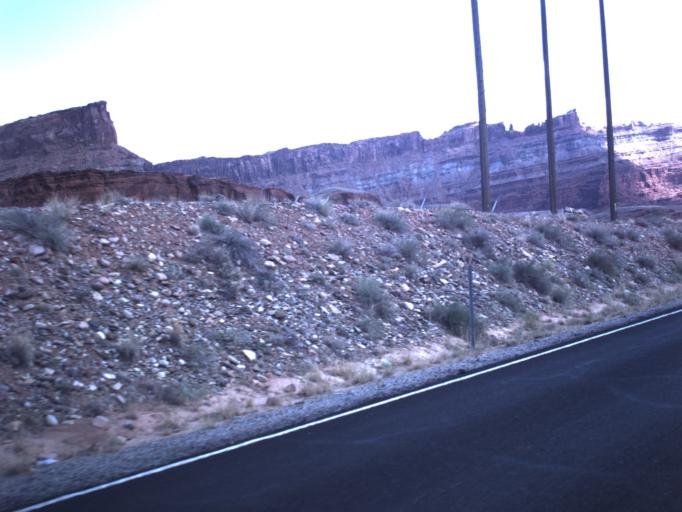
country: US
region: Utah
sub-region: Grand County
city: Moab
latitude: 38.5259
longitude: -109.6549
